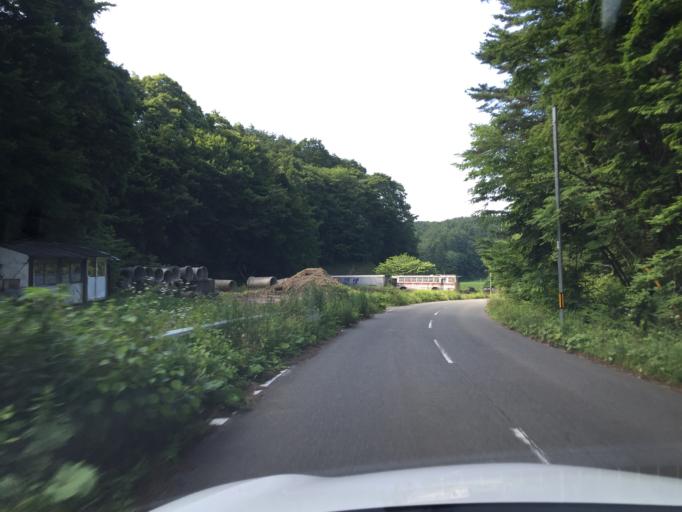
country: JP
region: Fukushima
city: Ishikawa
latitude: 37.1593
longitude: 140.6301
